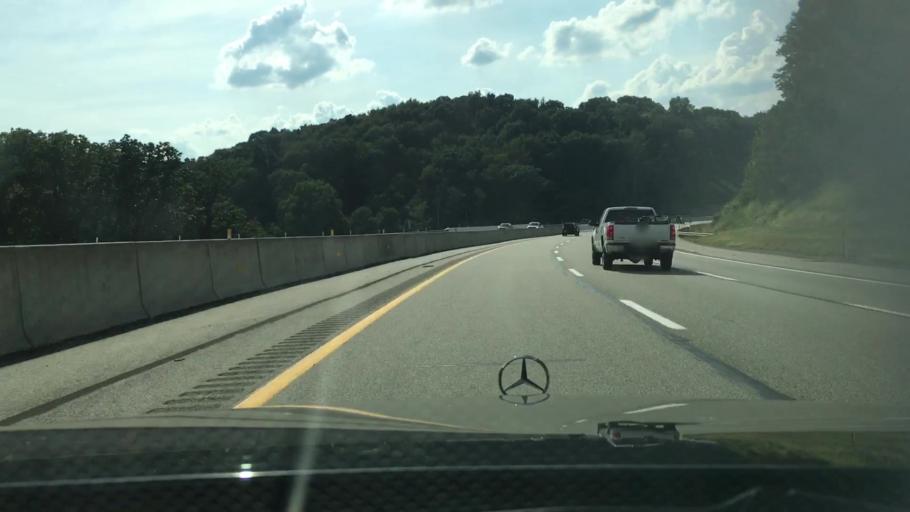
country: US
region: Pennsylvania
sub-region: Butler County
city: Mars
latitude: 40.6431
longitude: -80.0264
